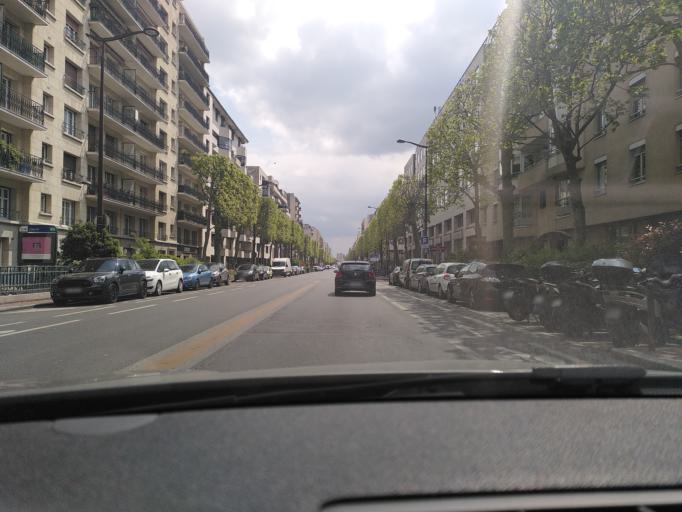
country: FR
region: Ile-de-France
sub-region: Departement du Val-de-Marne
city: Charenton-le-Pont
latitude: 48.8274
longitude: 2.4045
